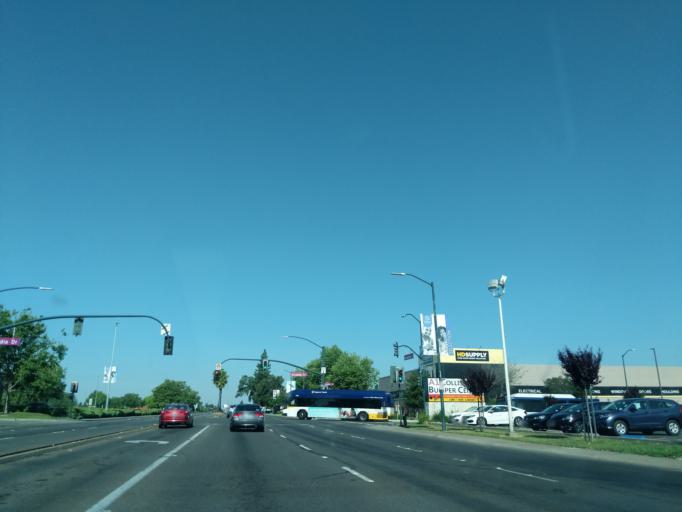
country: US
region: California
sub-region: Sacramento County
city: Citrus Heights
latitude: 38.6785
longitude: -121.2664
